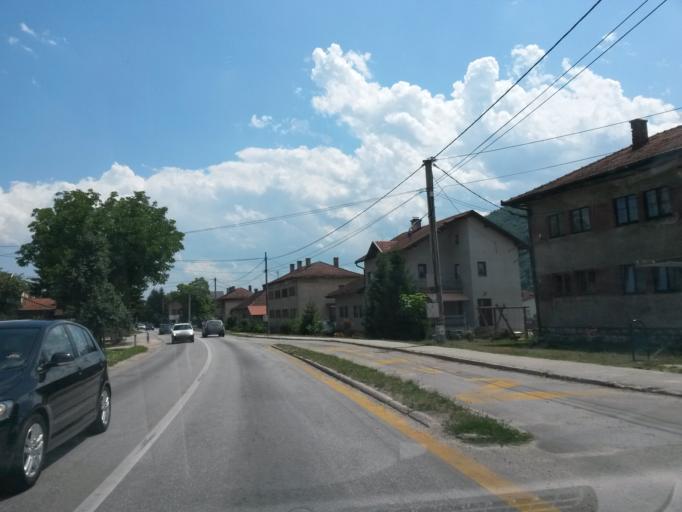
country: BA
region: Federation of Bosnia and Herzegovina
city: Vitez
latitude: 44.1918
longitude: 17.7343
